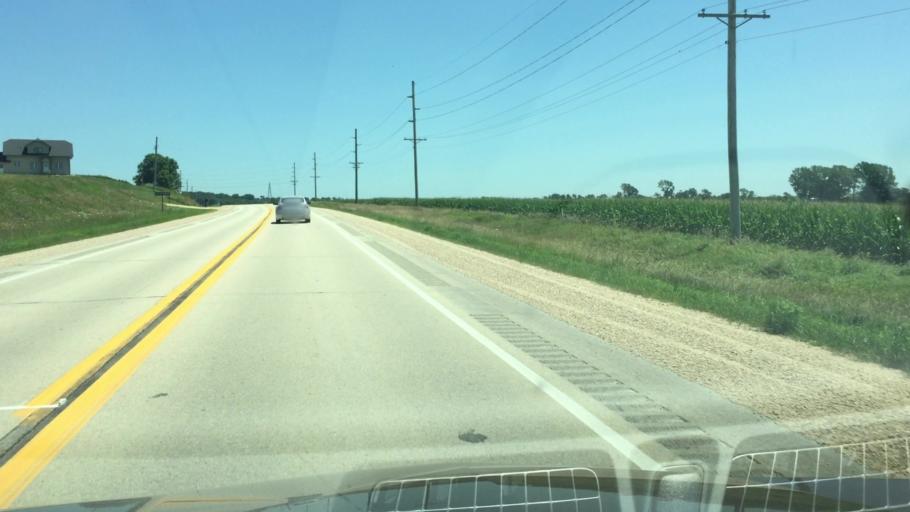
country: US
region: Iowa
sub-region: Jackson County
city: Maquoketa
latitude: 42.0671
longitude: -90.7812
